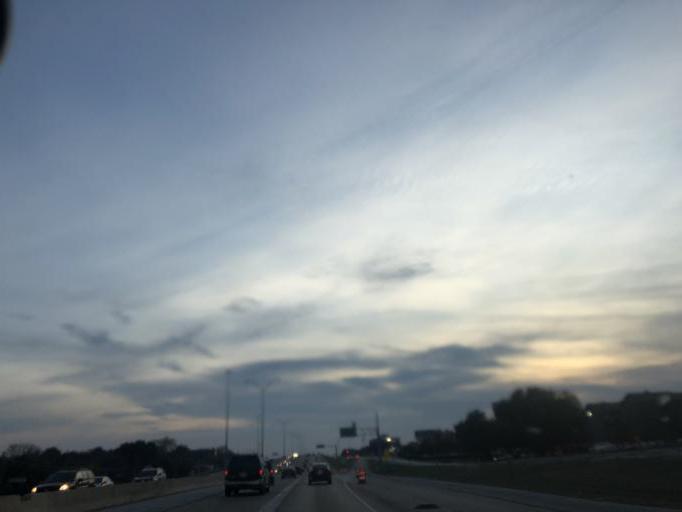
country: US
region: Texas
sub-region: Dallas County
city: Duncanville
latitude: 32.6815
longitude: -96.8527
